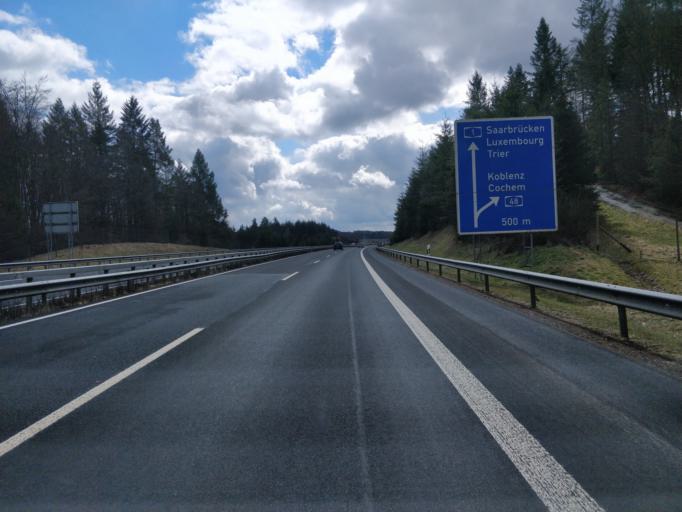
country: DE
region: Rheinland-Pfalz
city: Darscheid
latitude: 50.2006
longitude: 6.8913
